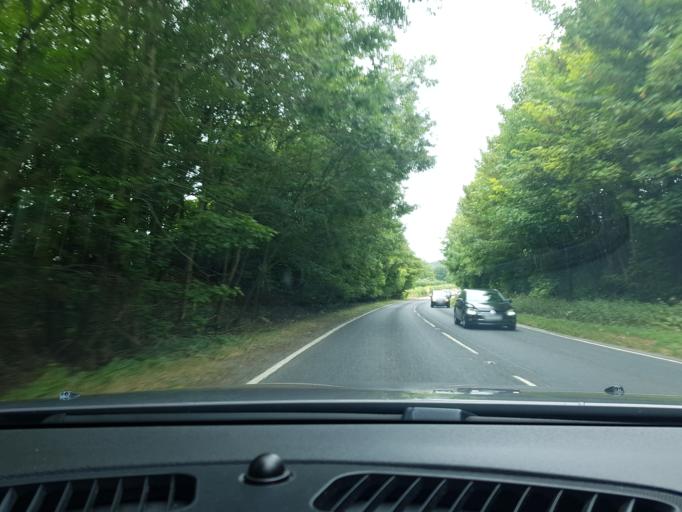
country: GB
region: England
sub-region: Hampshire
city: Tadley
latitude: 51.2913
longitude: -1.1662
